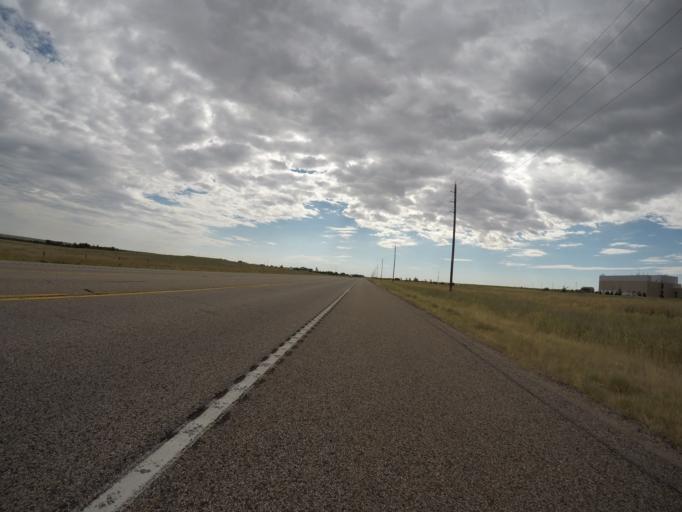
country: US
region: Wyoming
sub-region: Laramie County
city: Cheyenne
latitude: 41.1315
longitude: -104.9001
